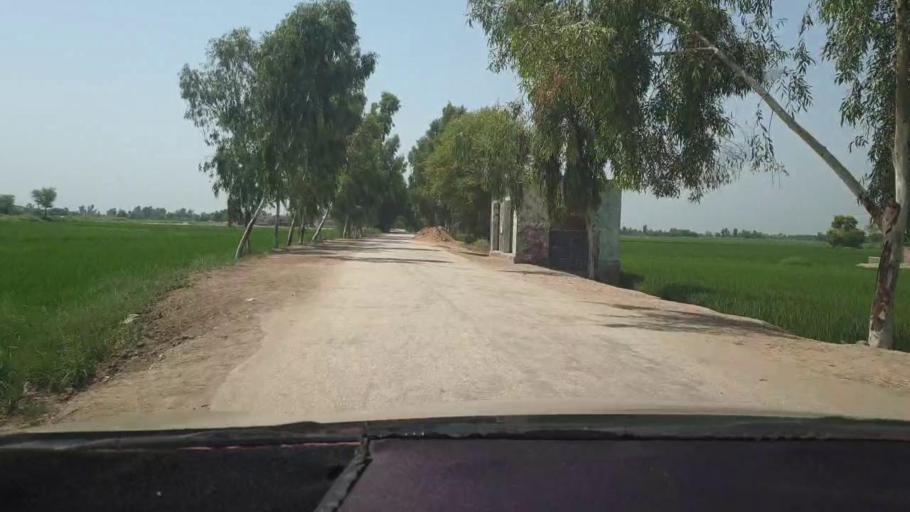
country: PK
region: Sindh
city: Miro Khan
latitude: 27.6718
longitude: 68.0588
